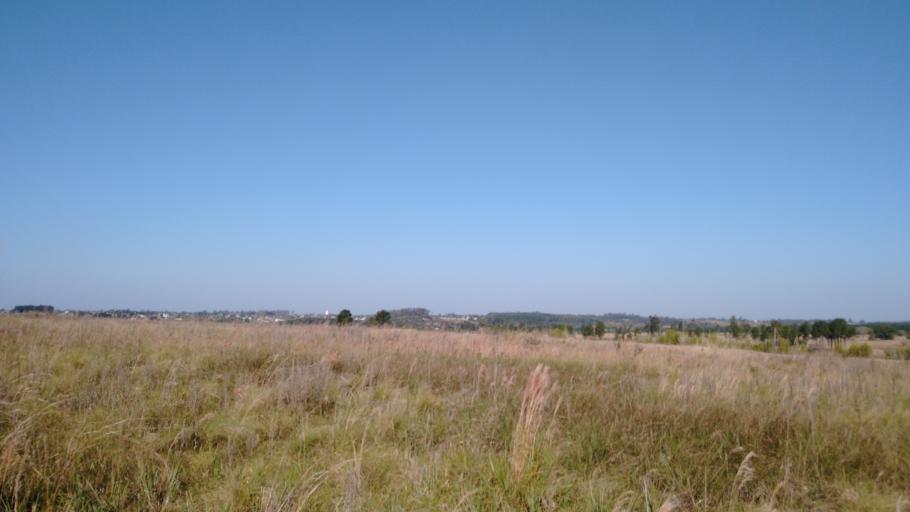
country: AR
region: Misiones
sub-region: Departamento de Capital
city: Posadas
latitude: -27.4115
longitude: -55.9747
